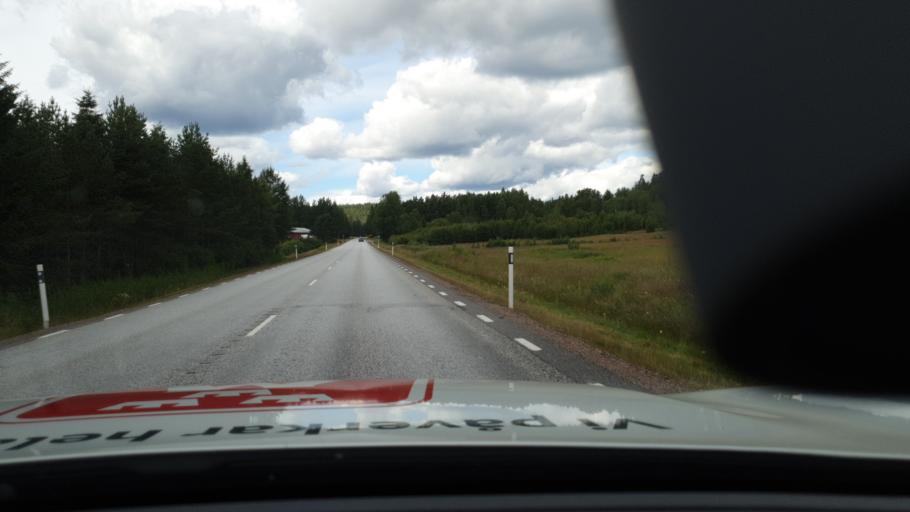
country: SE
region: Vaermland
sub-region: Storfors Kommun
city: Storfors
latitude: 59.5032
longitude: 14.3152
